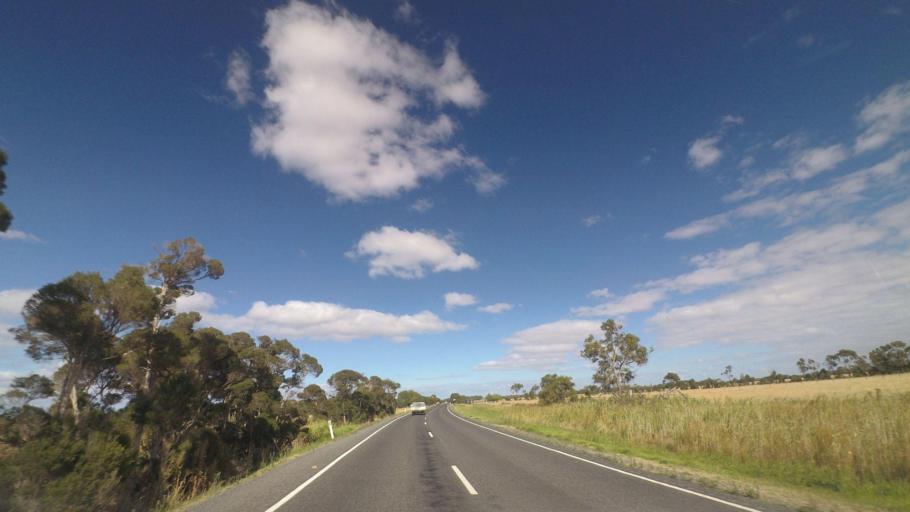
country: AU
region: Victoria
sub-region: Cardinia
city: Koo-Wee-Rup
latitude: -38.1852
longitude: 145.5457
